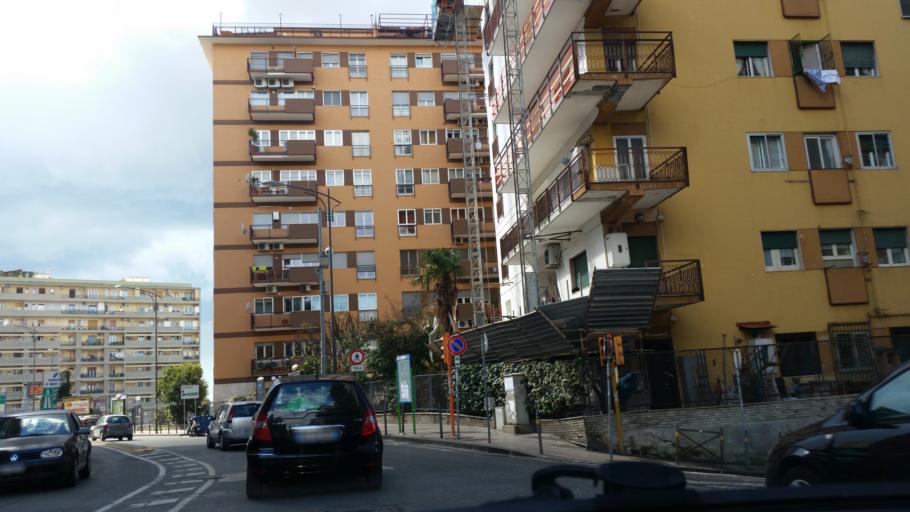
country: IT
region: Campania
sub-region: Provincia di Napoli
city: Napoli
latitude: 40.8430
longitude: 14.2201
